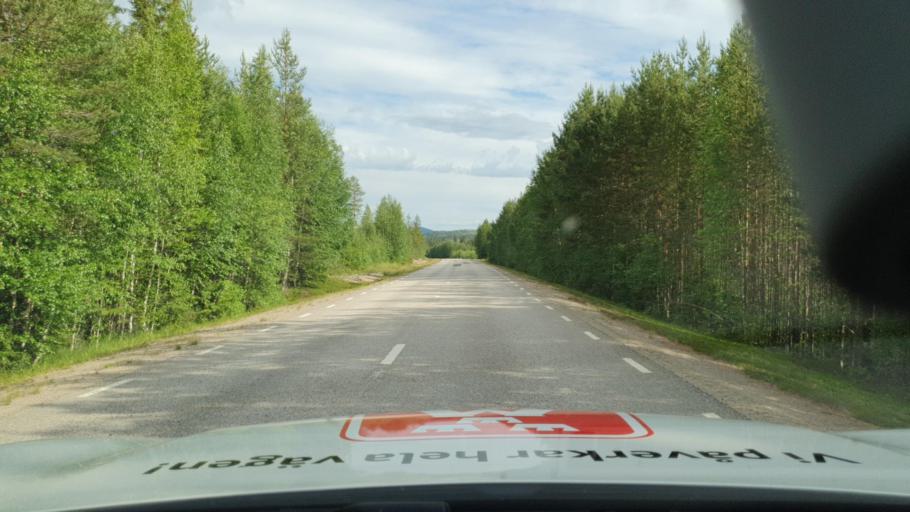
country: NO
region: Hedmark
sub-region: Trysil
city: Innbygda
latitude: 60.9405
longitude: 12.4762
